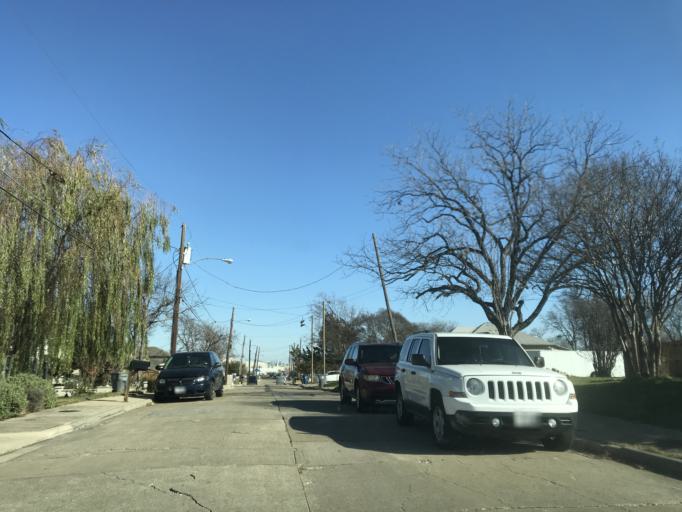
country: US
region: Texas
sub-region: Dallas County
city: Cockrell Hill
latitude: 32.7690
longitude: -96.9078
